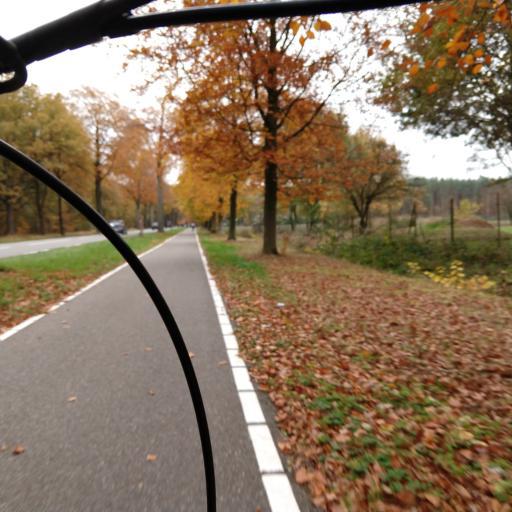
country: BE
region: Flanders
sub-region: Provincie Antwerpen
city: Stabroek
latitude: 51.3873
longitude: 4.3657
